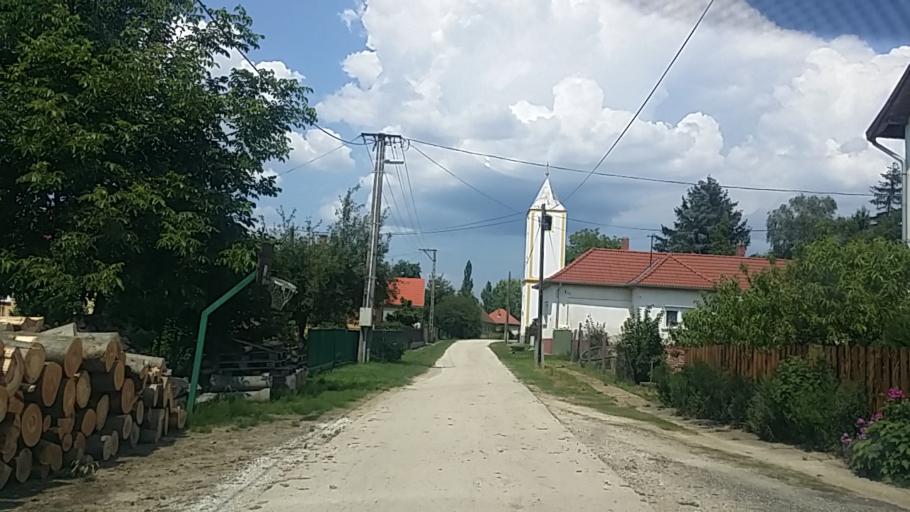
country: HR
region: Medimurska
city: Podturen
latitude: 46.5304
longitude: 16.5855
